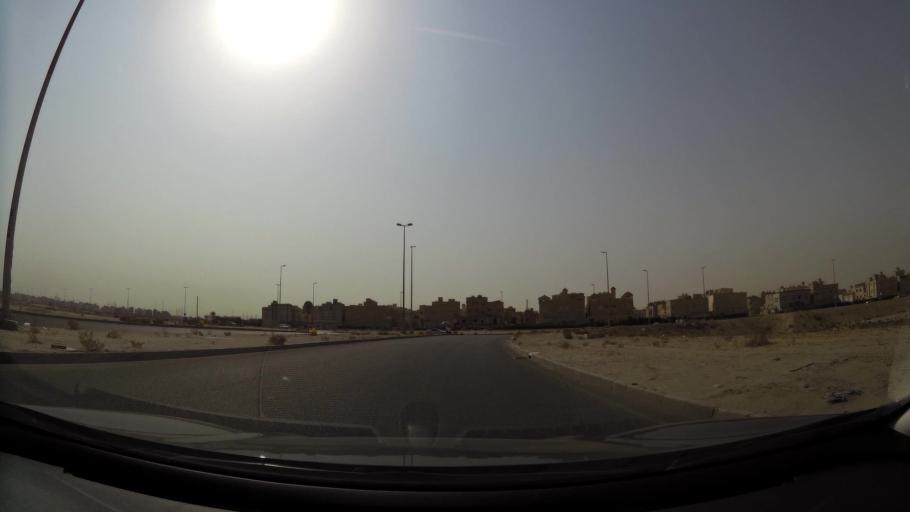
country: KW
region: Muhafazat al Jahra'
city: Al Jahra'
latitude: 29.3428
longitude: 47.7746
